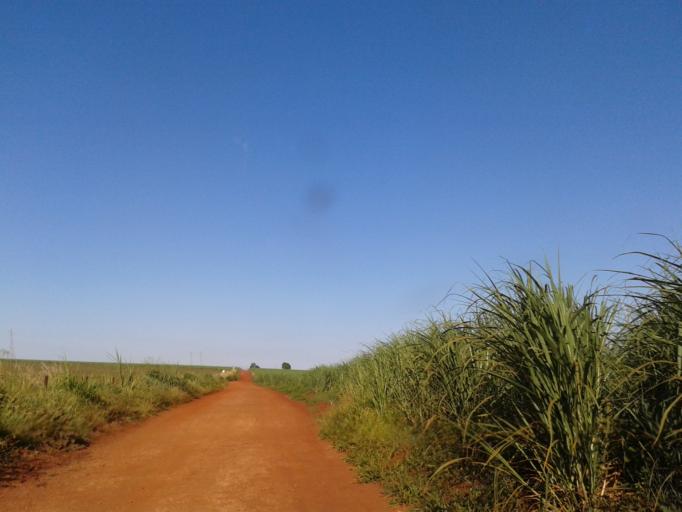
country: BR
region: Minas Gerais
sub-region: Centralina
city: Centralina
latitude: -18.6722
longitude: -49.2744
